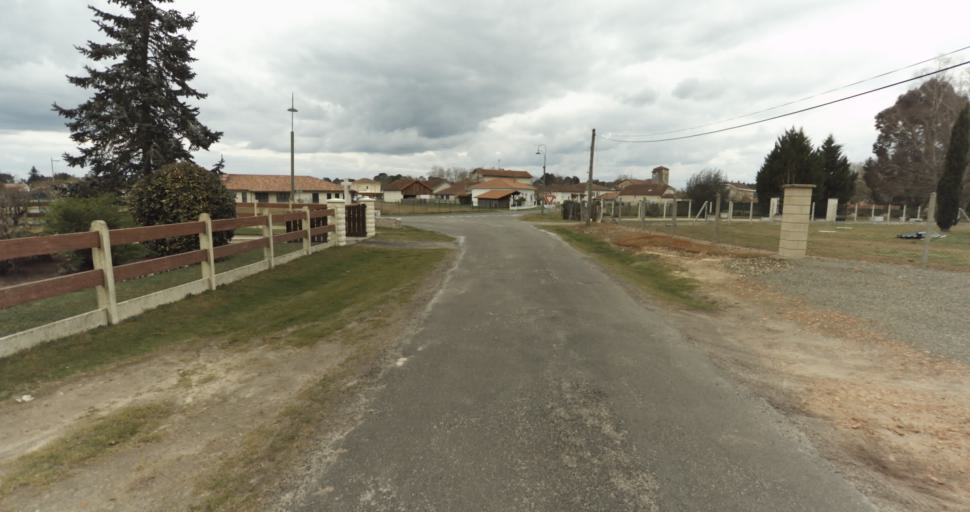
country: FR
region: Aquitaine
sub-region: Departement des Landes
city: Sarbazan
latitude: 44.0181
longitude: -0.3143
